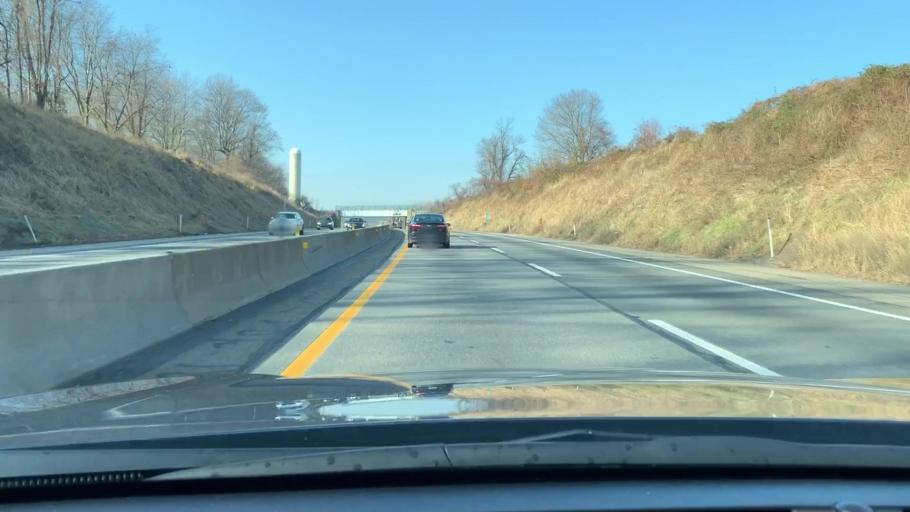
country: US
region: Pennsylvania
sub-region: Chester County
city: Downingtown
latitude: 40.0836
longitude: -75.7116
